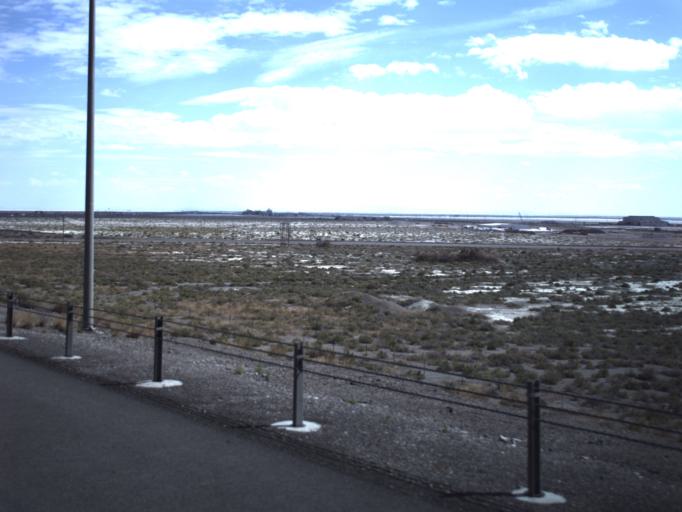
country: US
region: Utah
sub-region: Tooele County
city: Wendover
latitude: 40.7438
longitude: -114.0245
